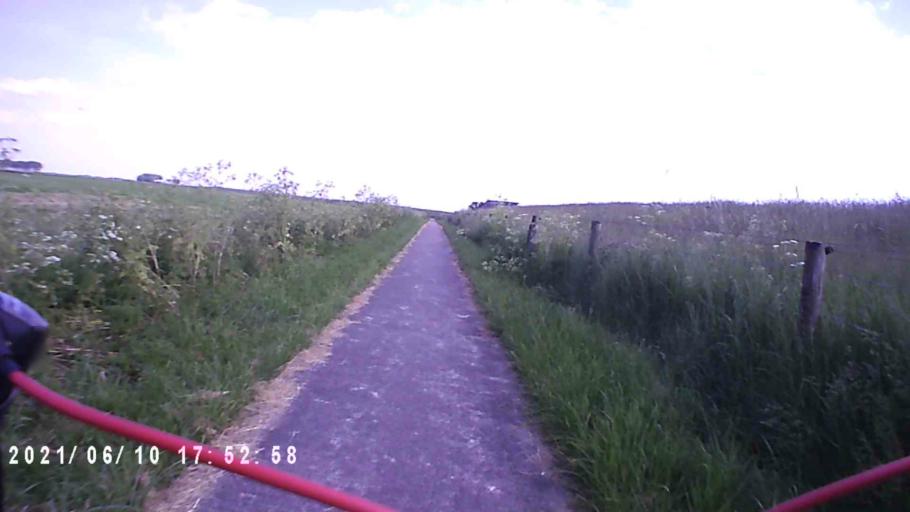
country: NL
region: Groningen
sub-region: Gemeente De Marne
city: Ulrum
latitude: 53.3271
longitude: 6.3204
